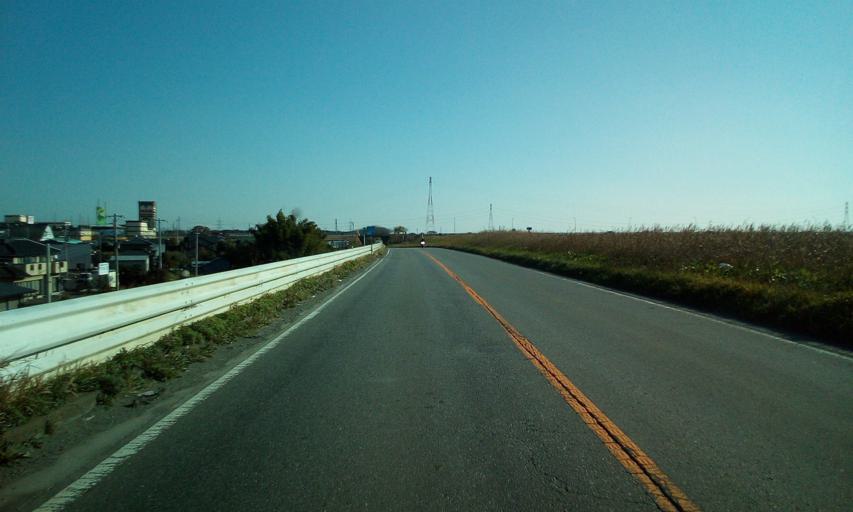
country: JP
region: Ibaraki
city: Sakai
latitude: 36.1033
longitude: 139.7918
